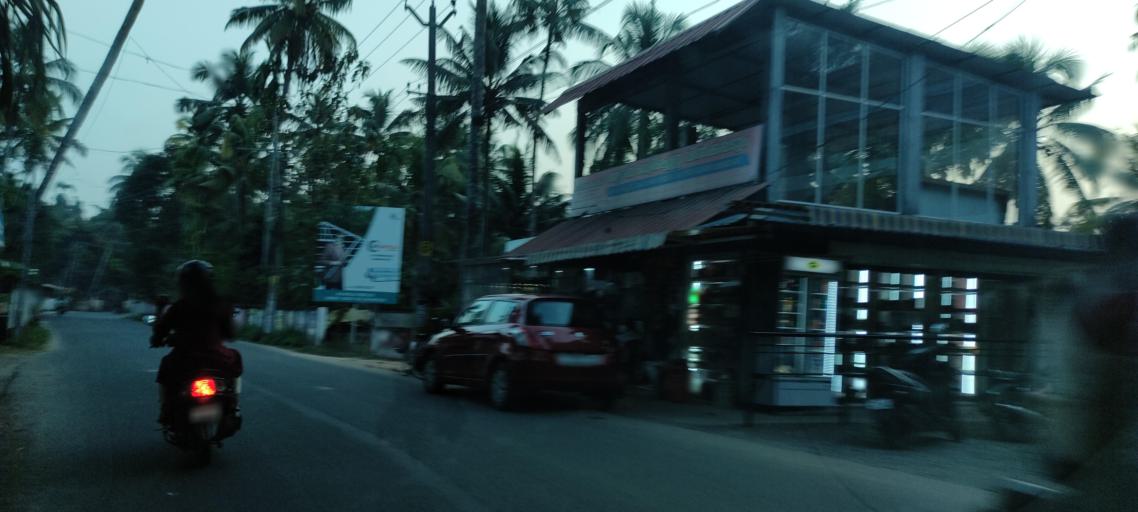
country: IN
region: Kerala
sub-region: Alappuzha
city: Kayankulam
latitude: 9.1251
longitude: 76.4961
